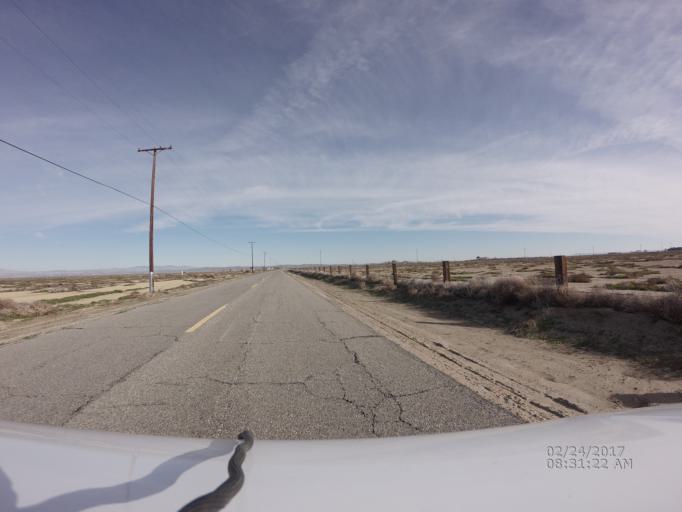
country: US
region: California
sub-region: Los Angeles County
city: Lancaster
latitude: 34.7543
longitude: -118.0235
